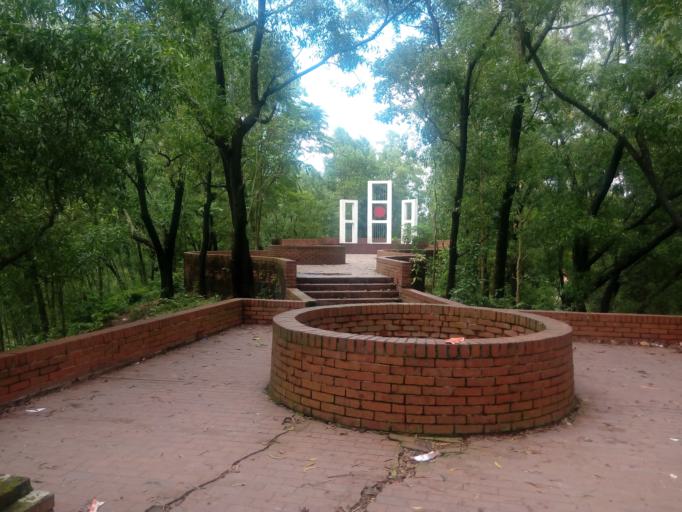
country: BD
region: Sylhet
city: Sylhet
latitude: 24.9231
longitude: 91.8316
